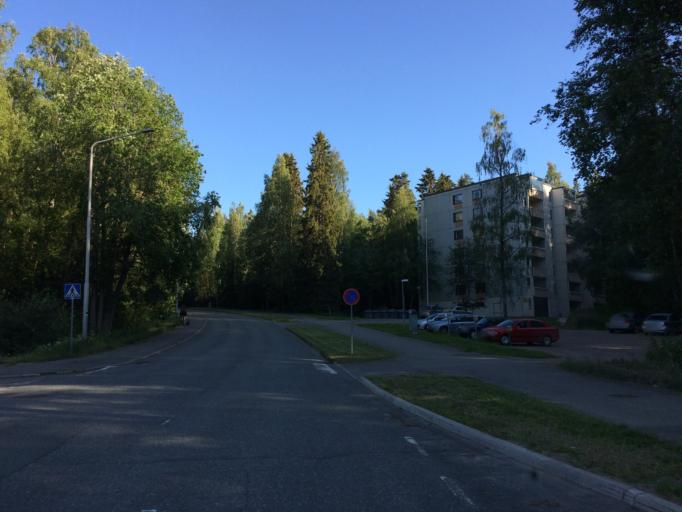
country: FI
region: Haeme
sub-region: Haemeenlinna
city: Haemeenlinna
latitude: 60.9844
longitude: 24.5175
